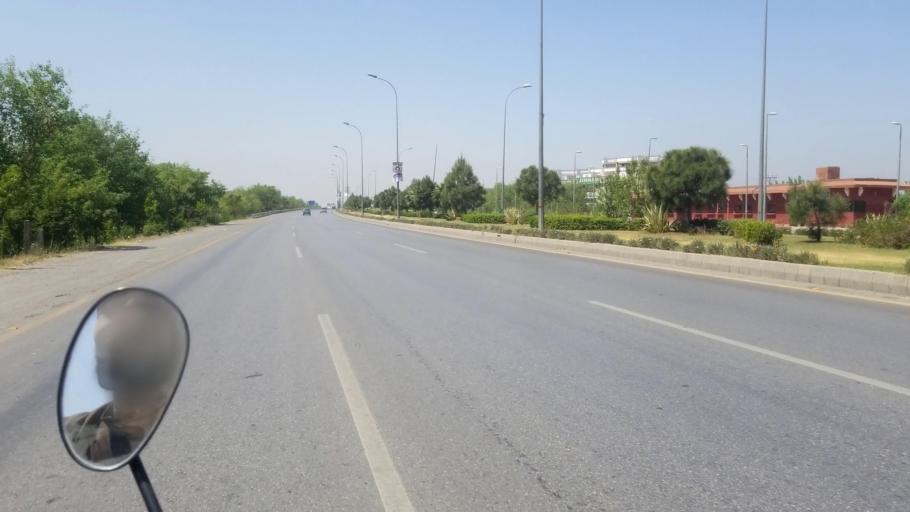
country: PK
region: Khyber Pakhtunkhwa
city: Peshawar
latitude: 34.0279
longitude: 71.6575
